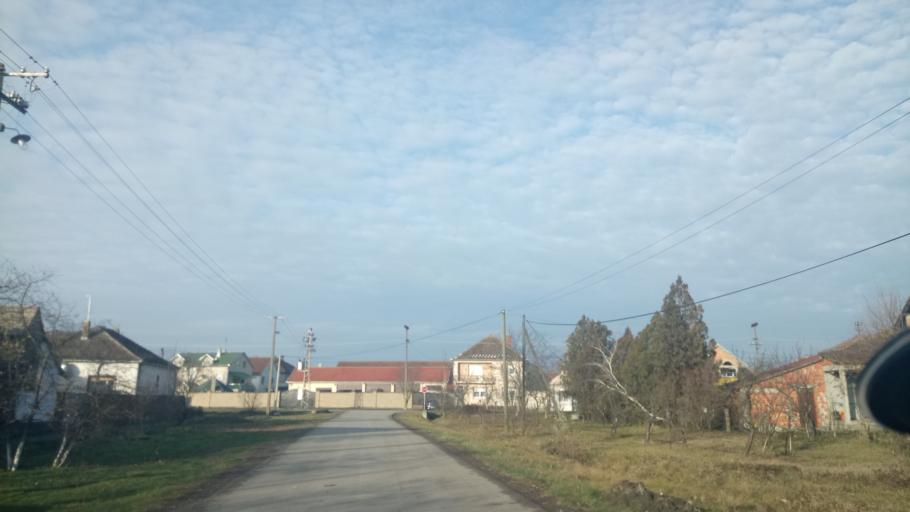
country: RS
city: Vojka
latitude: 44.9339
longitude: 20.1663
